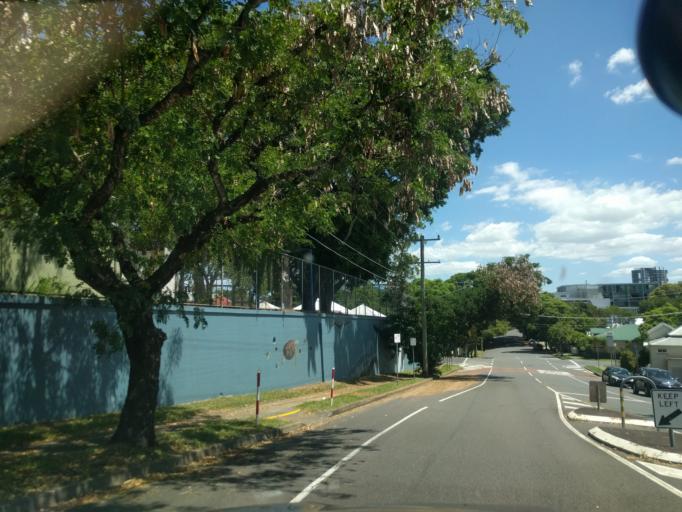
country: AU
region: Queensland
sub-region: Brisbane
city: Milton
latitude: -27.4602
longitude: 153.0094
